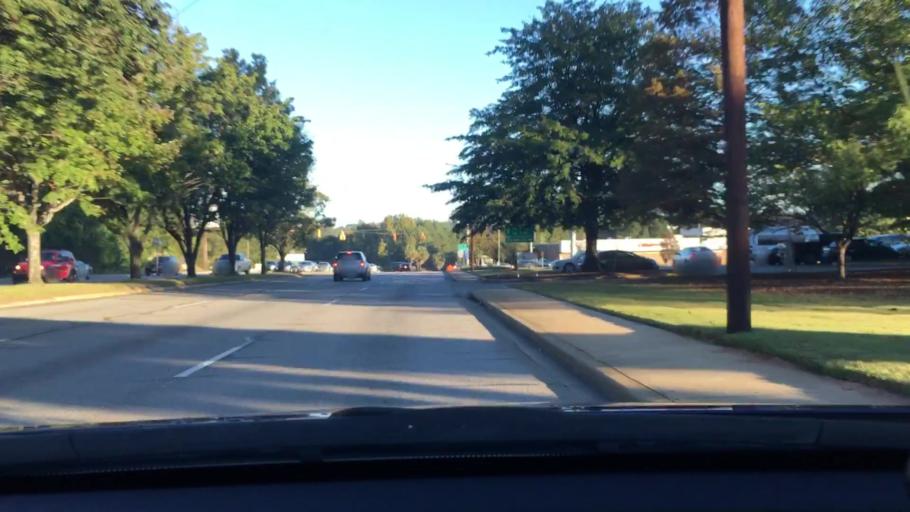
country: US
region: South Carolina
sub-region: Richland County
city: Columbia
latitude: 34.0228
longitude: -81.0375
